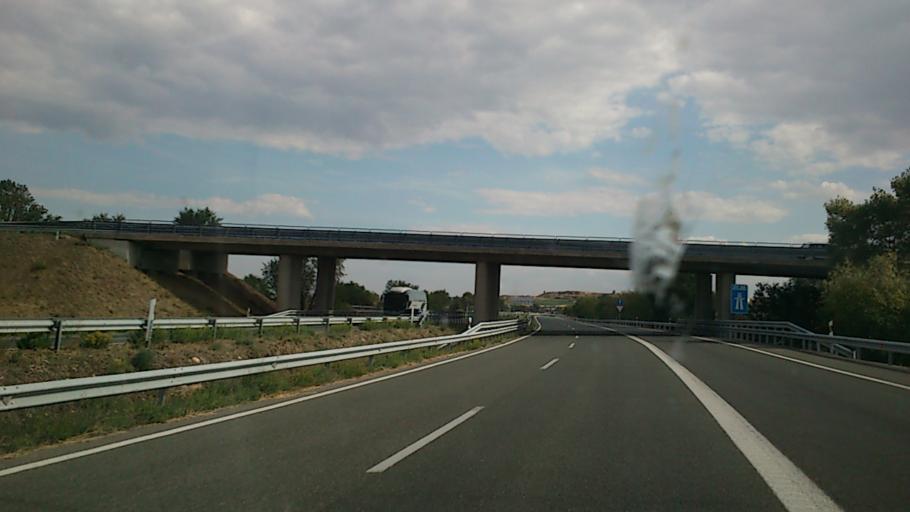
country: ES
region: La Rioja
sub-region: Provincia de La Rioja
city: Anguciana
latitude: 42.5599
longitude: -2.8760
